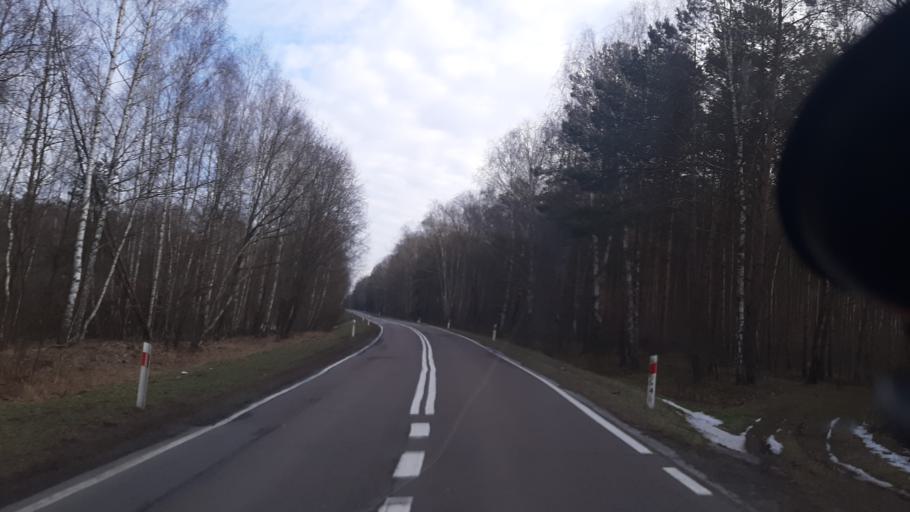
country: PL
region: Lublin Voivodeship
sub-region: Powiat lubartowski
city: Ostrow Lubelski
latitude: 51.4905
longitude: 22.7968
